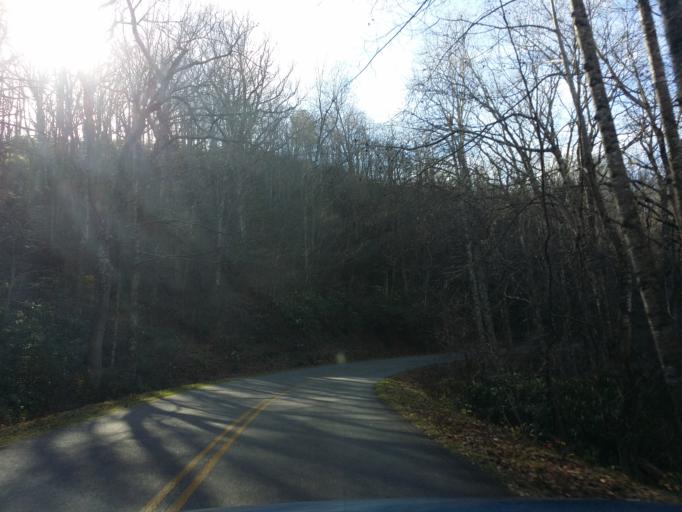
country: US
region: North Carolina
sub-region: McDowell County
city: West Marion
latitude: 35.7553
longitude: -82.1806
